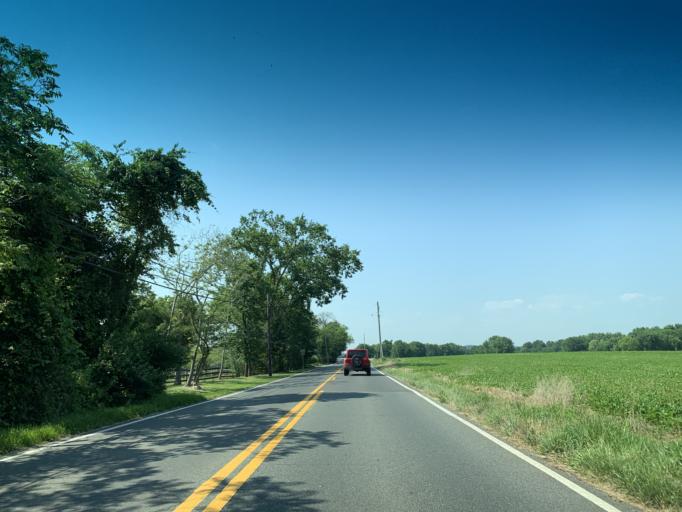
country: US
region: Maryland
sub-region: Montgomery County
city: Poolesville
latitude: 39.1290
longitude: -77.3840
